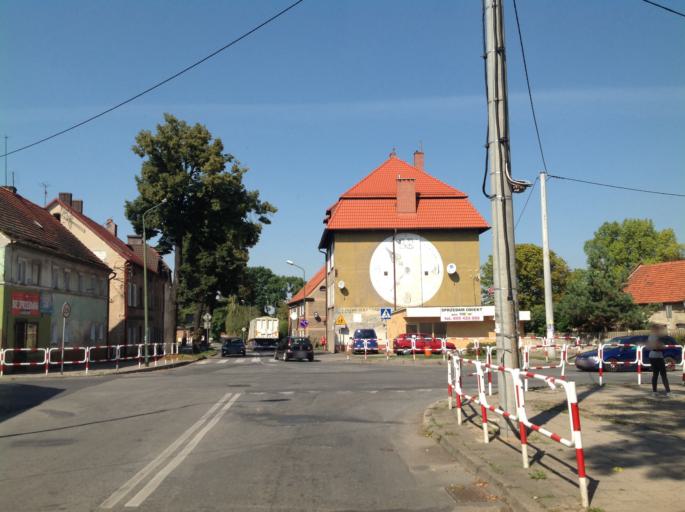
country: PL
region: Lower Silesian Voivodeship
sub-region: Powiat zabkowicki
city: Ziebice
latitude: 50.6026
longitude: 17.0449
